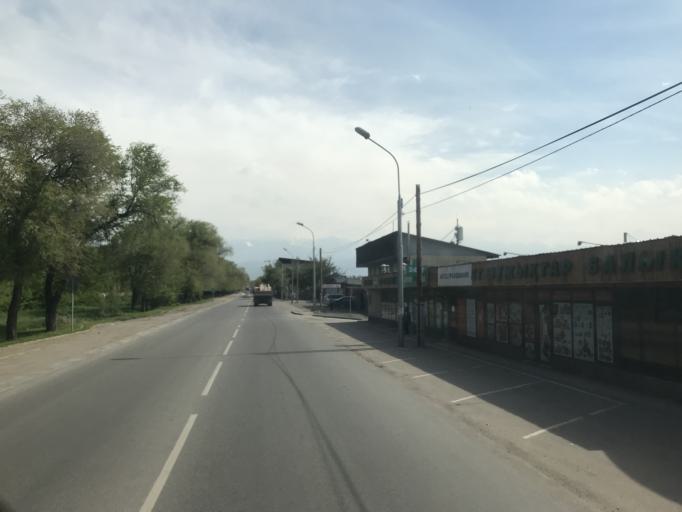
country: KZ
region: Almaty Qalasy
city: Almaty
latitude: 43.2469
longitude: 76.8040
